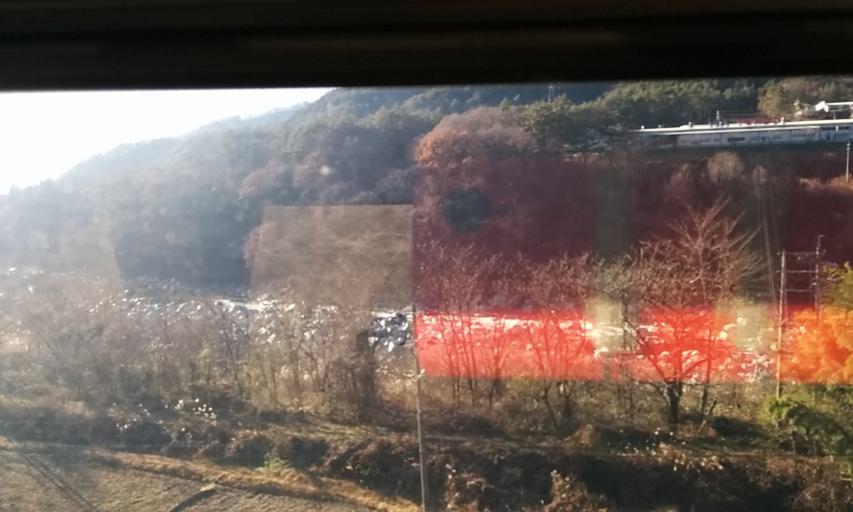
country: JP
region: Nagano
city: Iida
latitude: 35.7076
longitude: 137.7022
